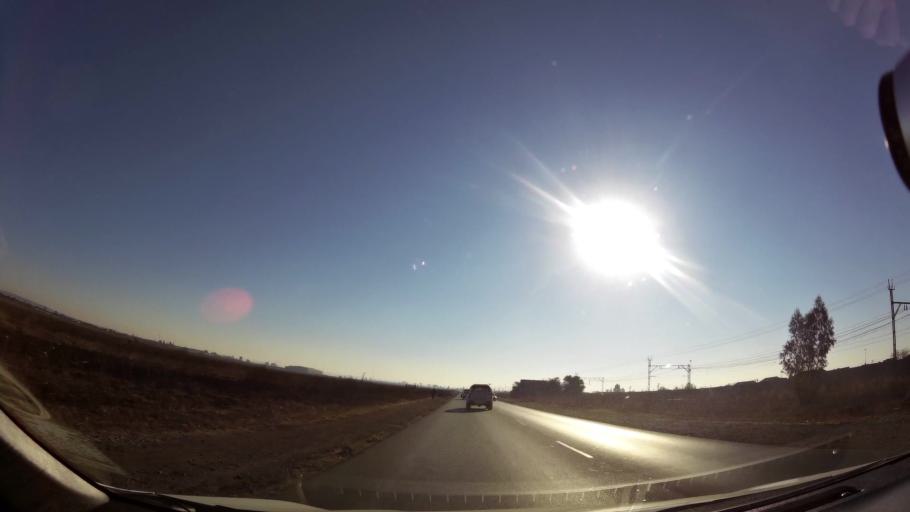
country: ZA
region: Gauteng
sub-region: Ekurhuleni Metropolitan Municipality
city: Germiston
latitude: -26.3405
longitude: 28.1324
